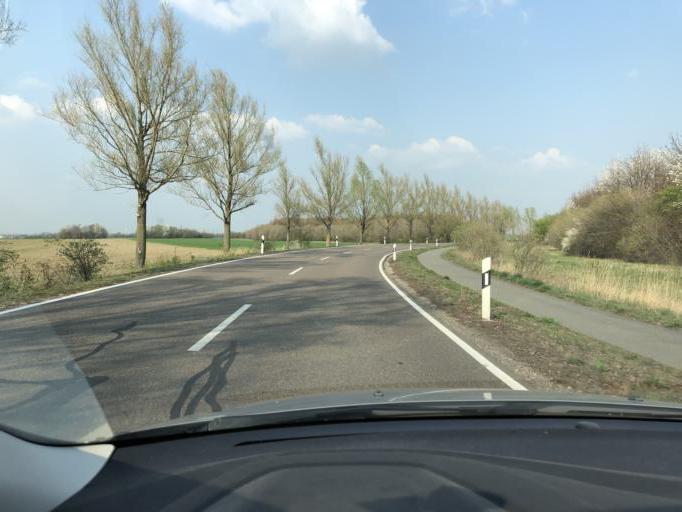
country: DE
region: Saxony
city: Zwochau
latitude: 51.4384
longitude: 12.2710
